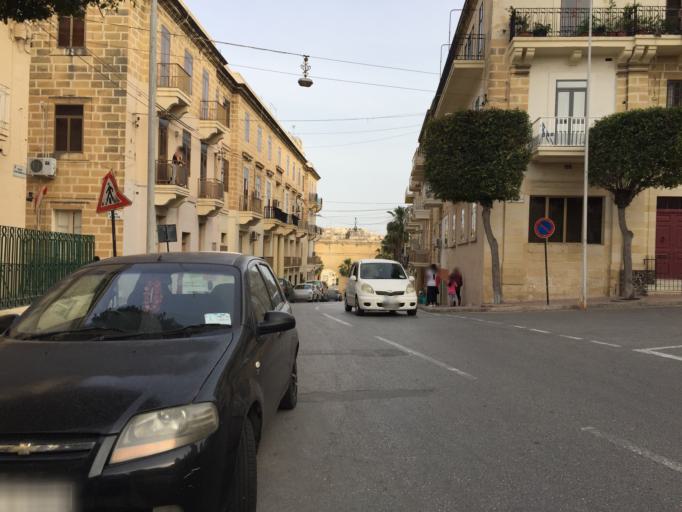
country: MT
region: L-Isla
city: Senglea
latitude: 35.8858
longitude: 14.5184
